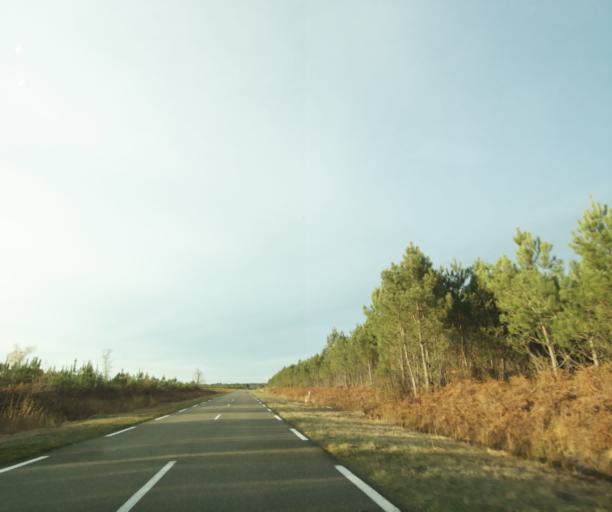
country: FR
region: Aquitaine
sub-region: Departement des Landes
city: Gabarret
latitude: 44.0772
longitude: -0.0685
